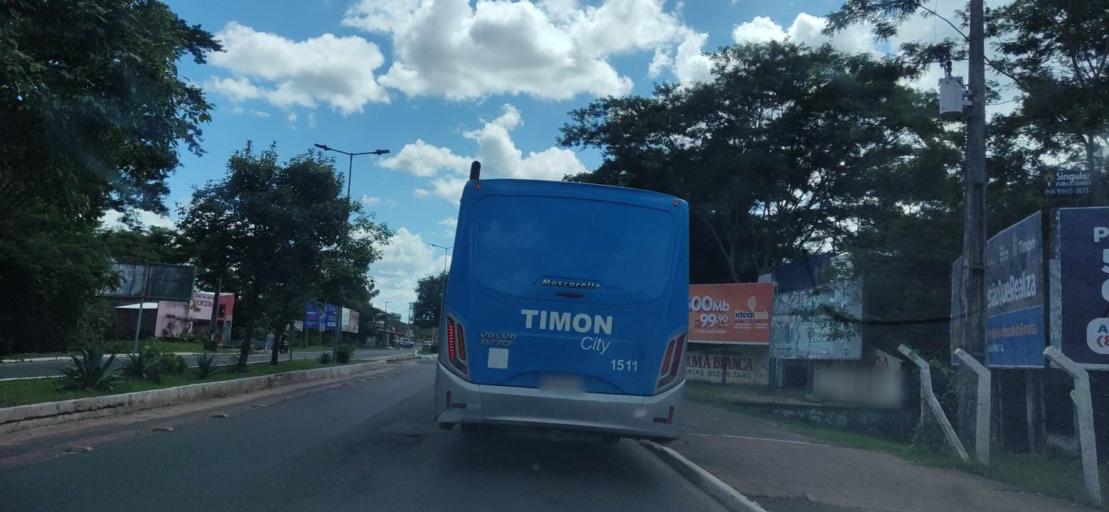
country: BR
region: Maranhao
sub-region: Timon
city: Timon
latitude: -5.0897
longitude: -42.8248
